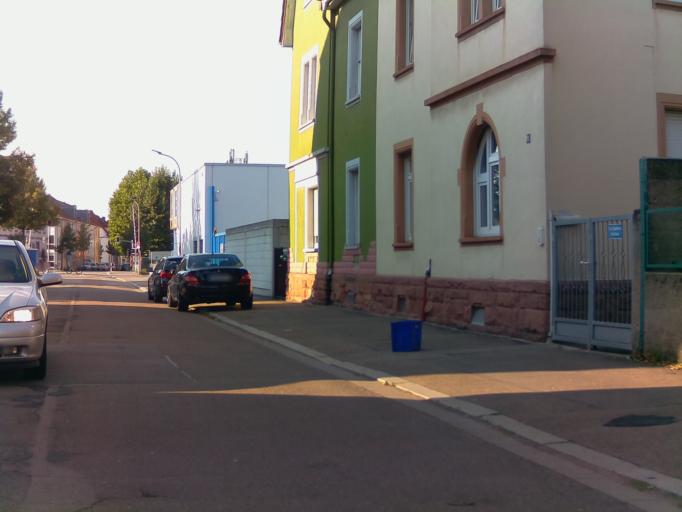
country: DE
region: Baden-Wuerttemberg
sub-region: Karlsruhe Region
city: Weinheim
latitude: 49.5572
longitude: 8.6688
